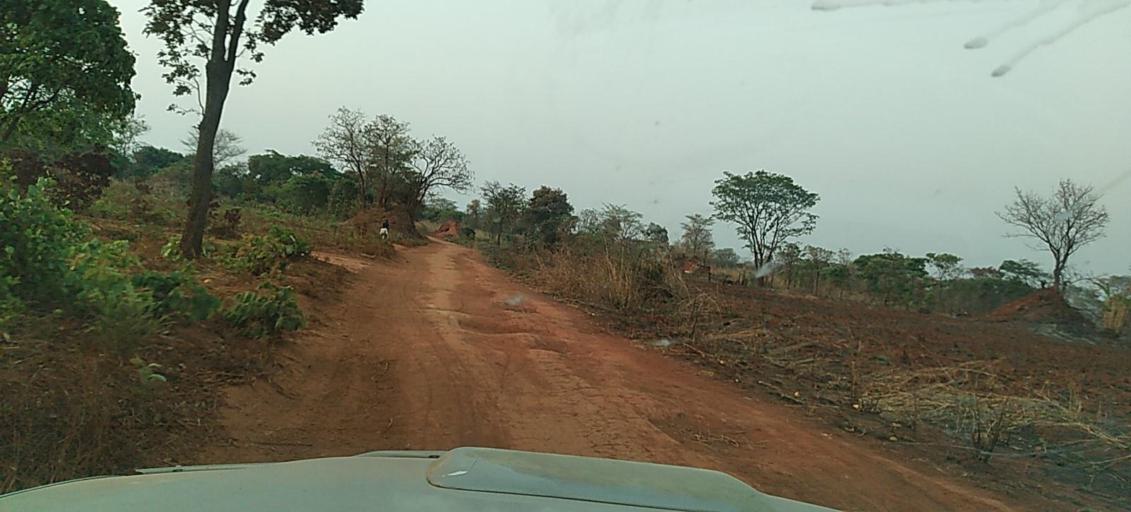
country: ZM
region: North-Western
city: Kasempa
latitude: -13.0630
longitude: 26.3818
